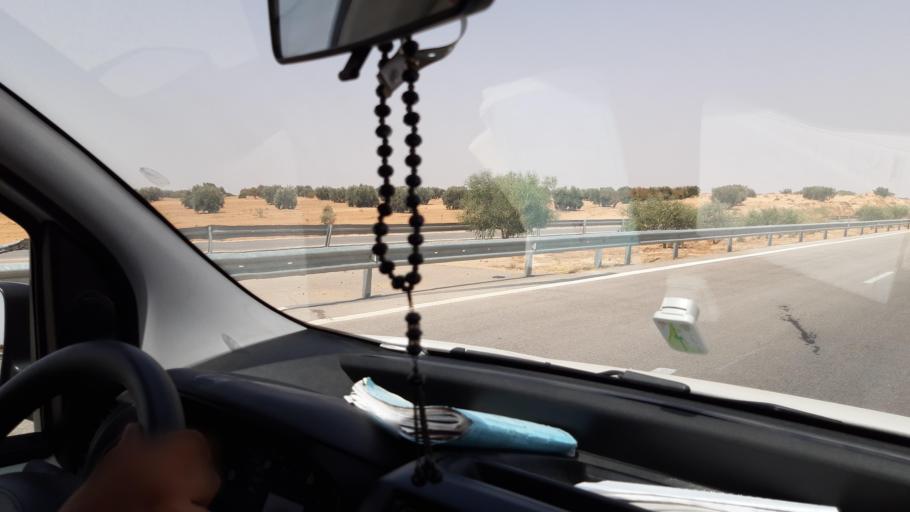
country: TN
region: Safaqis
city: Bi'r `Ali Bin Khalifah
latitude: 34.5260
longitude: 10.0831
